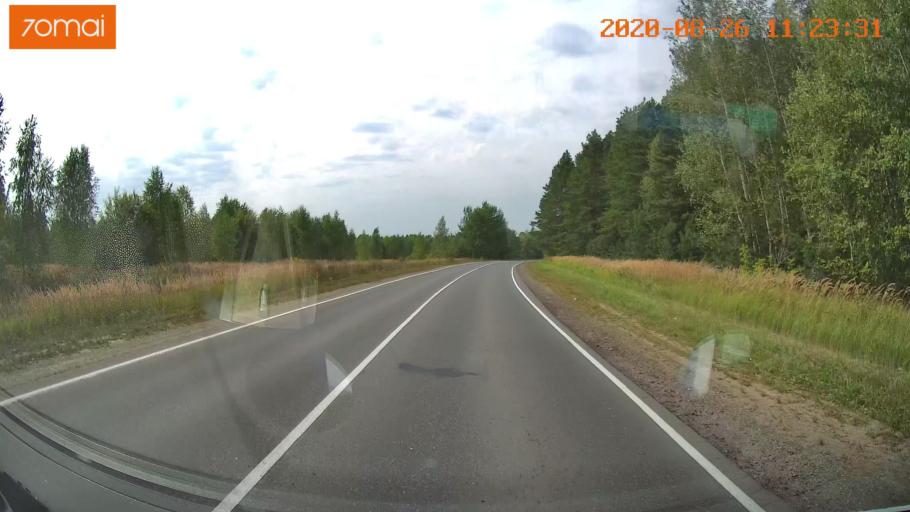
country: RU
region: Rjazan
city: Shilovo
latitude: 54.3513
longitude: 41.0091
